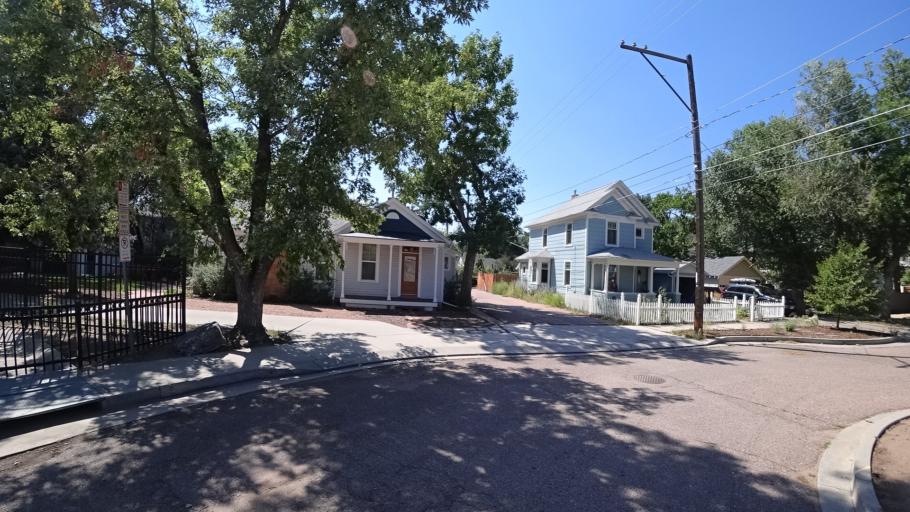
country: US
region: Colorado
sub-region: El Paso County
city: Colorado Springs
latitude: 38.8577
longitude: -104.8194
